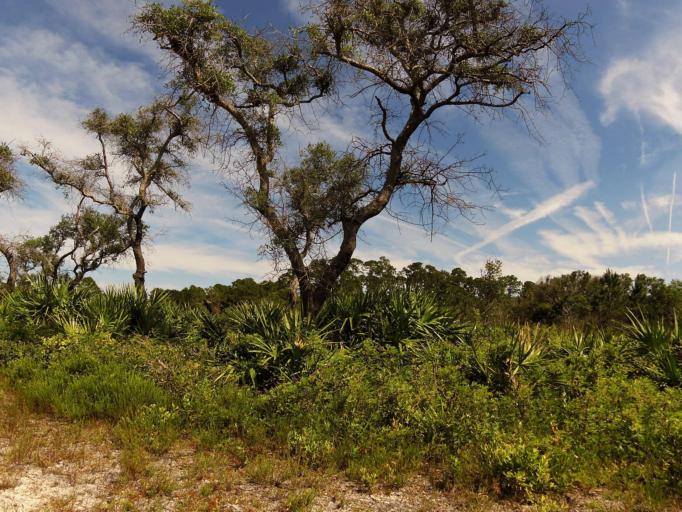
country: US
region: Florida
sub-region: Saint Johns County
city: Villano Beach
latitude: 30.0278
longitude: -81.3411
